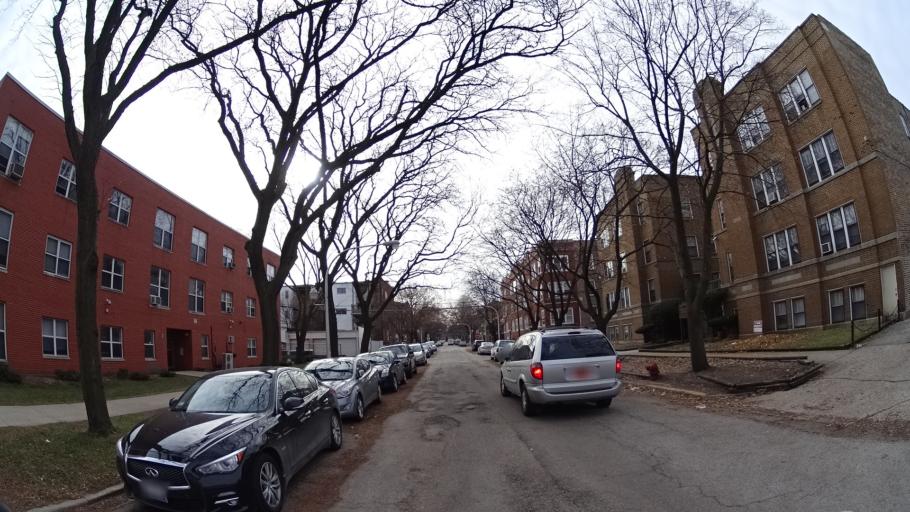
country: US
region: Illinois
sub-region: Cook County
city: Evanston
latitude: 42.0189
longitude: -87.6826
